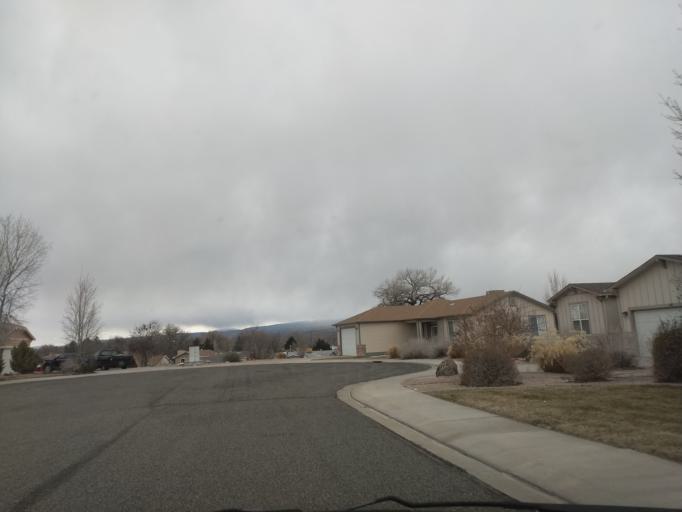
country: US
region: Colorado
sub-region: Mesa County
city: Fruitvale
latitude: 39.0880
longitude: -108.5220
